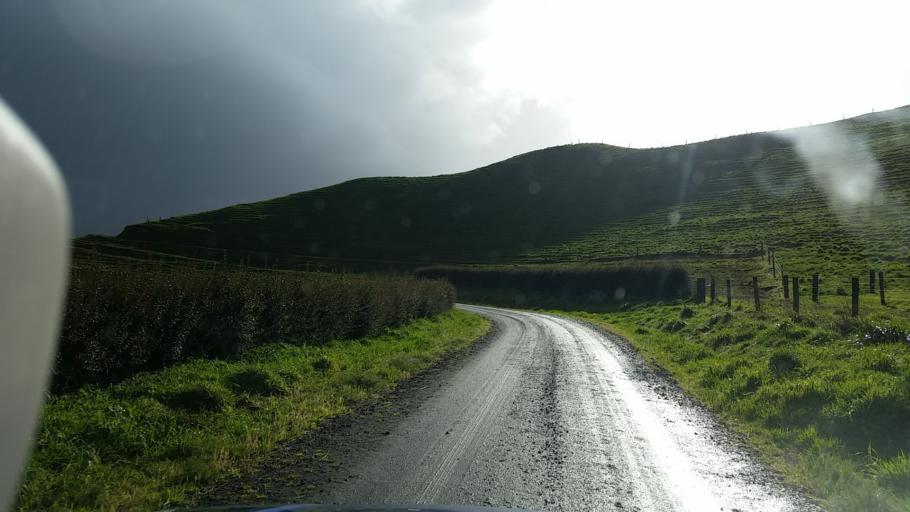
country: NZ
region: Taranaki
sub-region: South Taranaki District
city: Eltham
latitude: -39.3466
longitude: 174.4437
